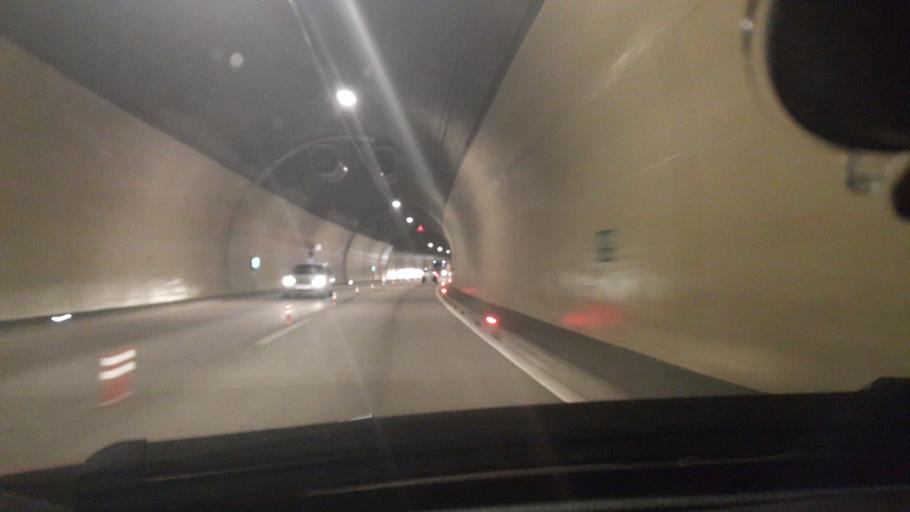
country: AT
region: Carinthia
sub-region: Klagenfurt am Woerthersee
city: Klagenfurt am Woerthersee
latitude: 46.6498
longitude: 14.3231
